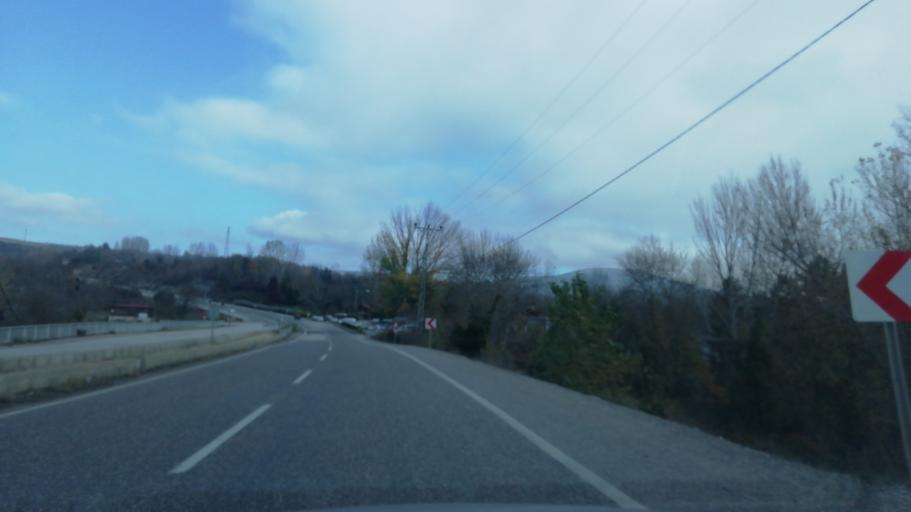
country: TR
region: Karabuk
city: Safranbolu
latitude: 41.2160
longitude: 32.7640
